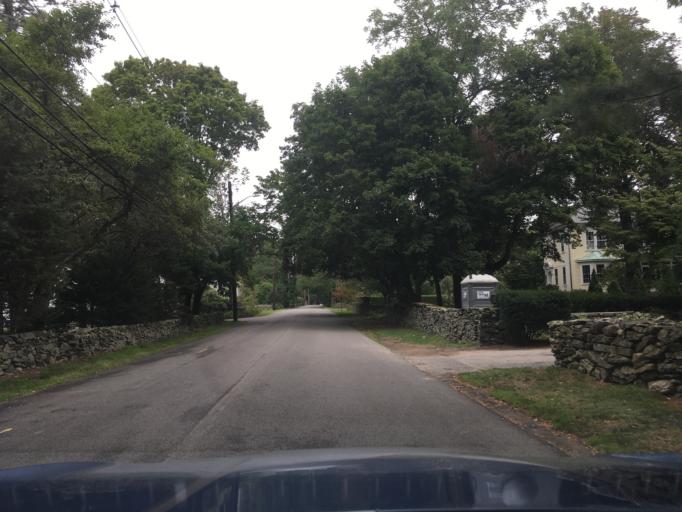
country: US
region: Rhode Island
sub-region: Bristol County
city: Warren
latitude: 41.7139
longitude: -71.3036
